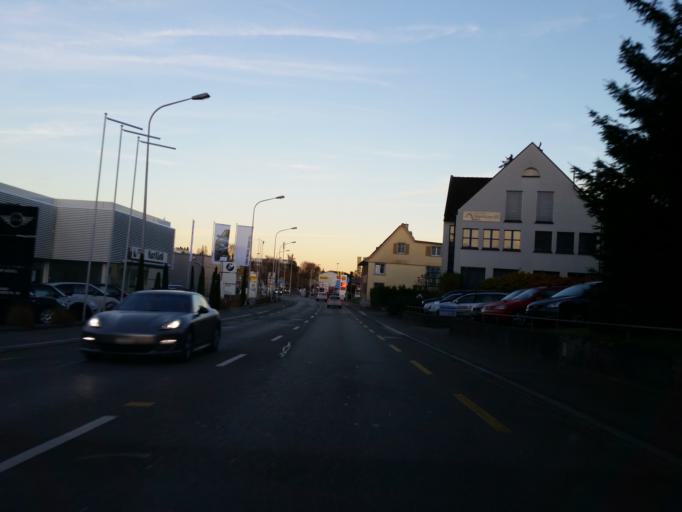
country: CH
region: Thurgau
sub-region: Kreuzlingen District
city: Bottighofen
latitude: 47.6393
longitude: 9.1981
